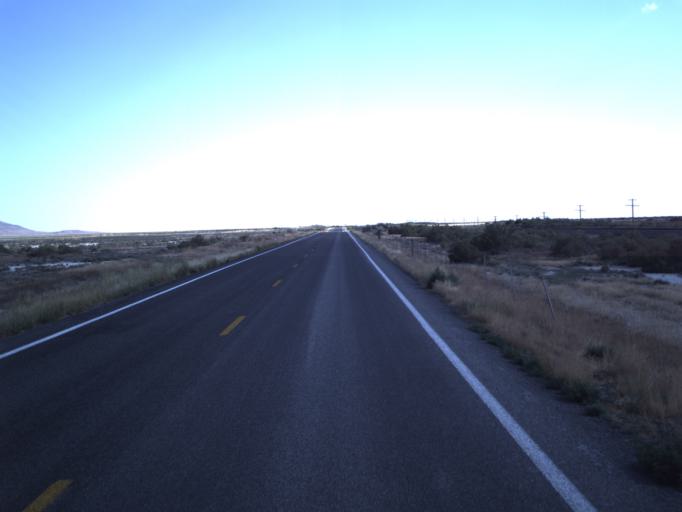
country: US
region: Utah
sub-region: Millard County
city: Delta
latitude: 38.9474
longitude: -112.8066
